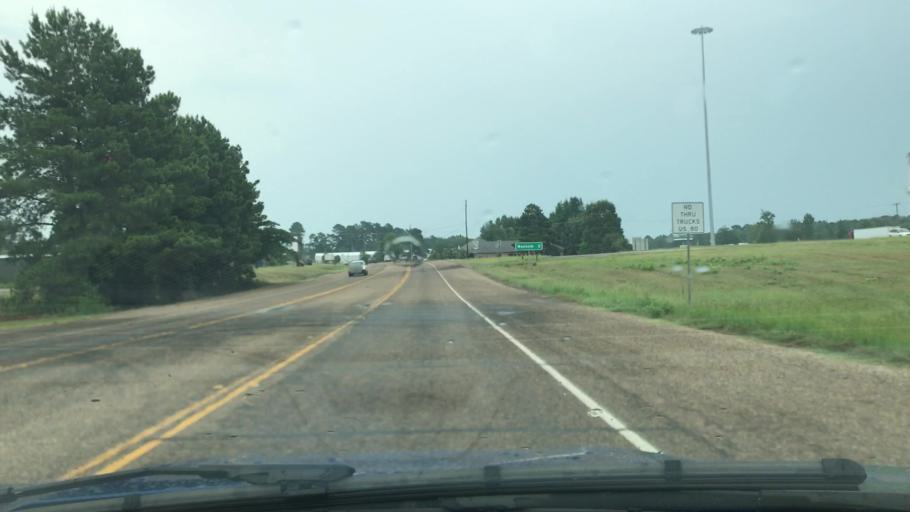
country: US
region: Texas
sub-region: Harrison County
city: Waskom
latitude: 32.4793
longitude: -94.0849
